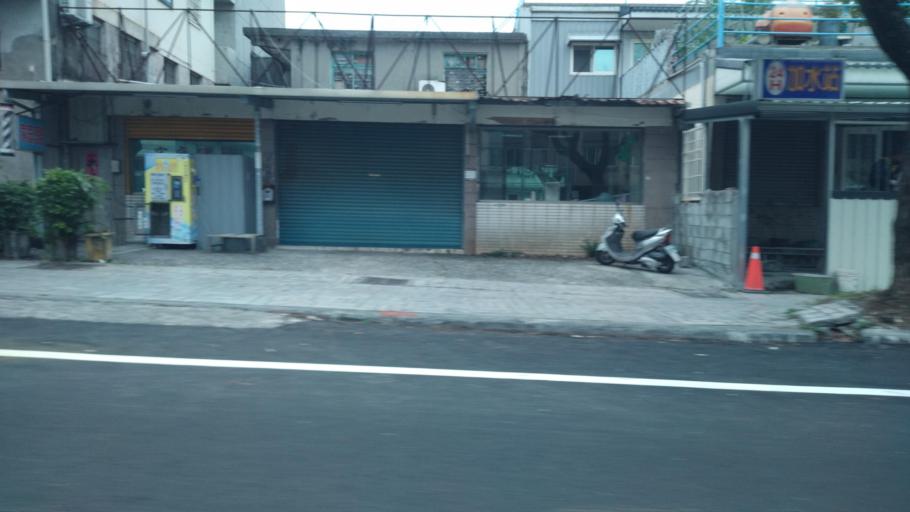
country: TW
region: Taiwan
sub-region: Hualien
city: Hualian
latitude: 24.0044
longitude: 121.6189
